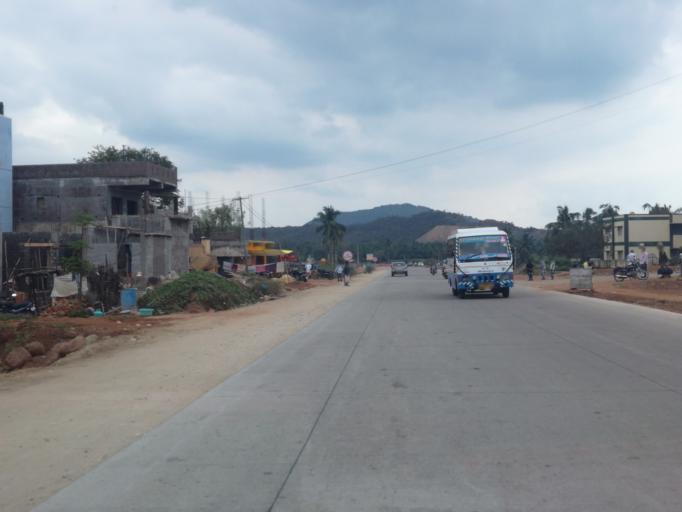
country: IN
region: Andhra Pradesh
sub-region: Chittoor
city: Ramapuram
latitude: 13.1001
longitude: 79.1251
